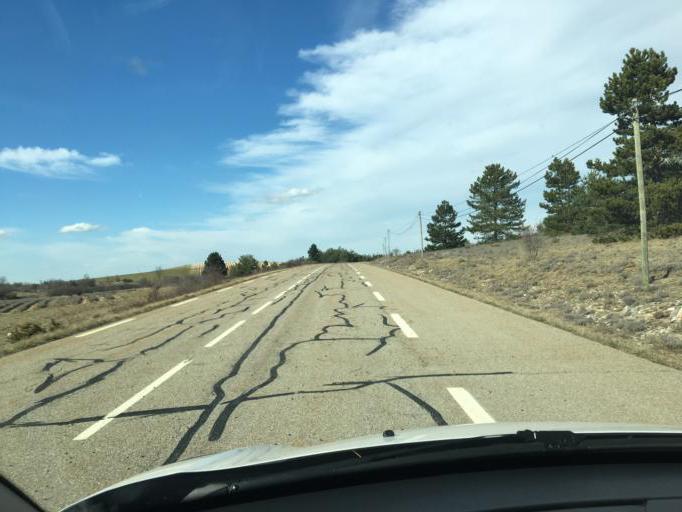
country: FR
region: Provence-Alpes-Cote d'Azur
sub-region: Departement du Vaucluse
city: Saint-Saturnin-les-Apt
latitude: 43.9924
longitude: 5.4771
